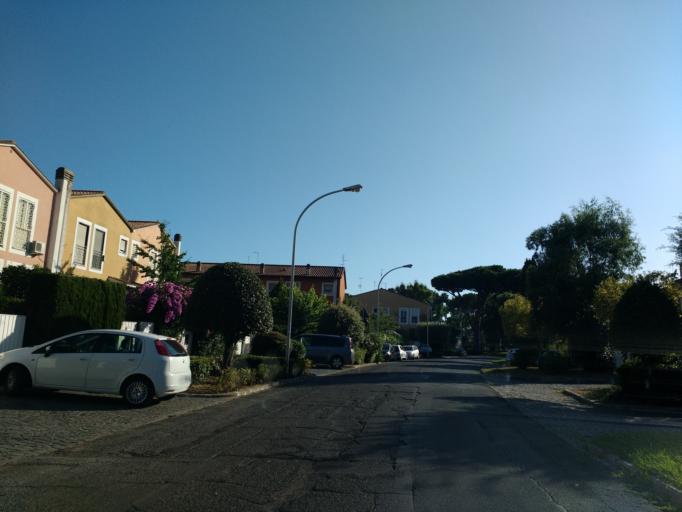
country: IT
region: Latium
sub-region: Citta metropolitana di Roma Capitale
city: Acilia-Castel Fusano-Ostia Antica
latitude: 41.7564
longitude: 12.3631
